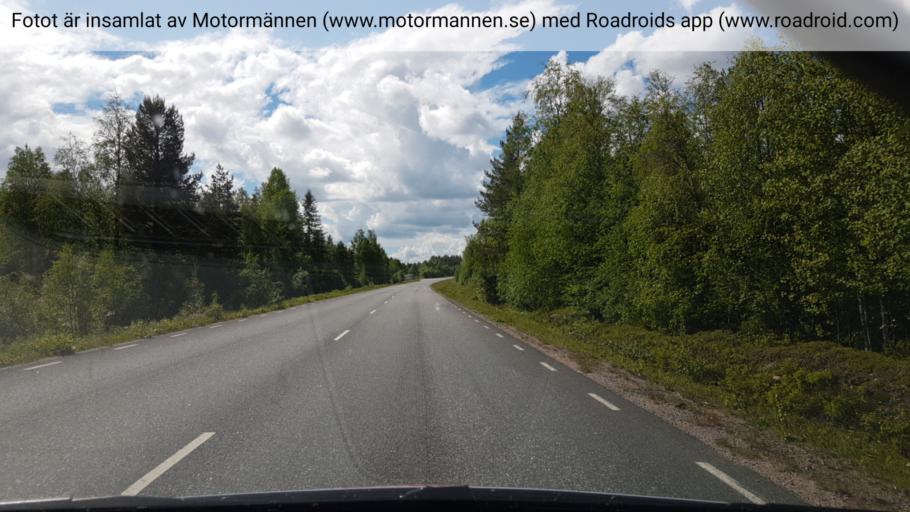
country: FI
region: Lapland
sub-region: Torniolaakso
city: Ylitornio
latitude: 66.3390
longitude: 23.6448
